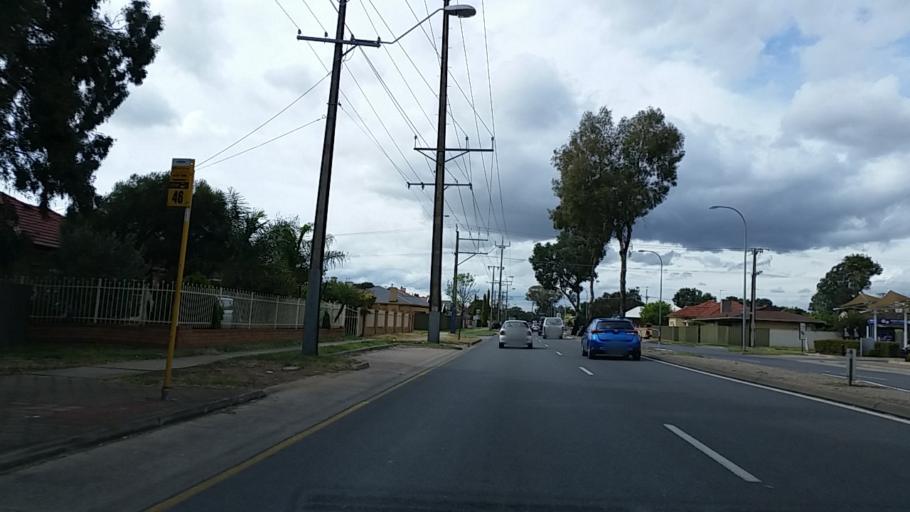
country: AU
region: South Australia
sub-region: Salisbury
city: Salisbury
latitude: -34.7670
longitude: 138.6372
